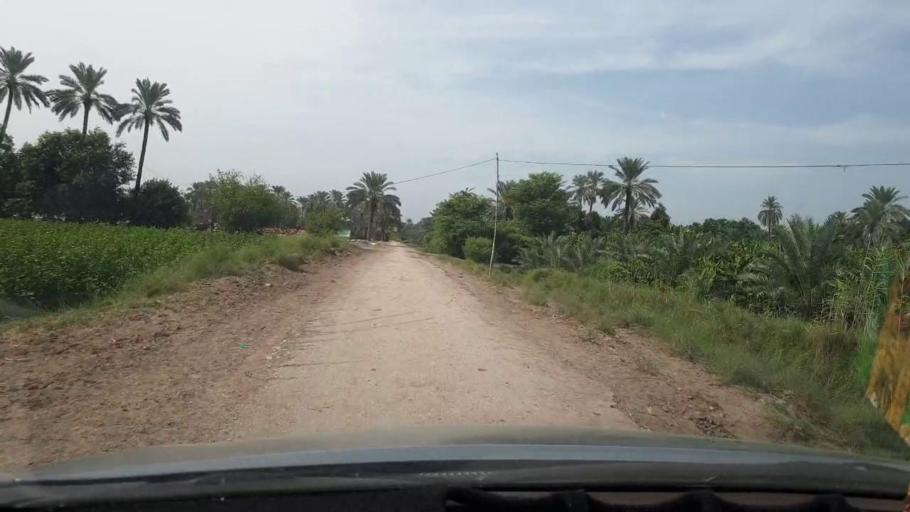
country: PK
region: Sindh
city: Khairpur
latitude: 27.5045
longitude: 68.7560
